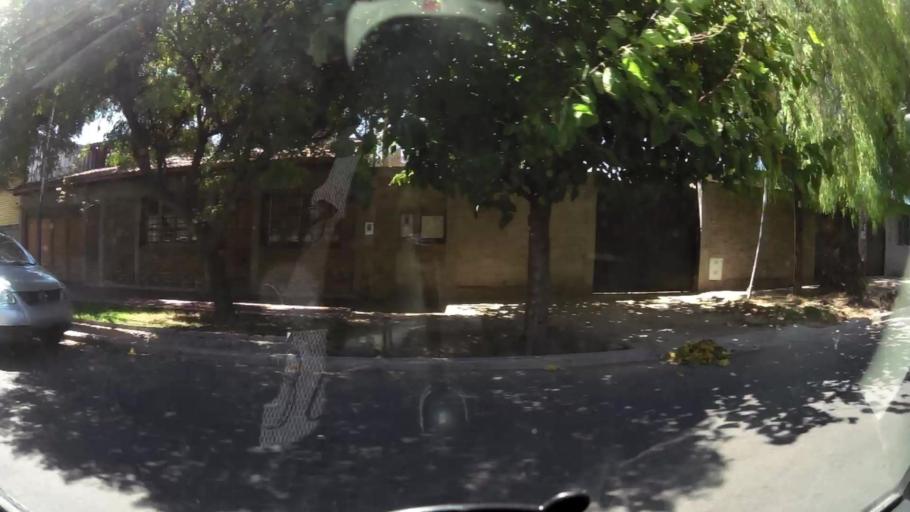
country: AR
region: Mendoza
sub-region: Departamento de Godoy Cruz
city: Godoy Cruz
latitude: -32.9126
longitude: -68.8641
